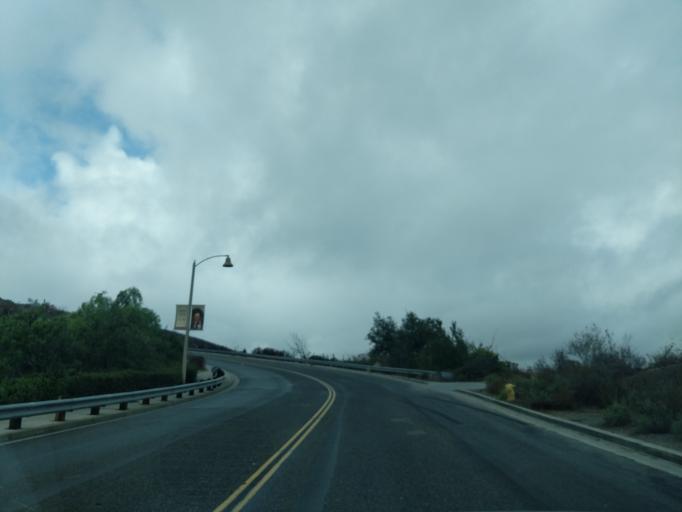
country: US
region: California
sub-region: Ventura County
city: Simi Valley
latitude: 34.2582
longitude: -118.8141
